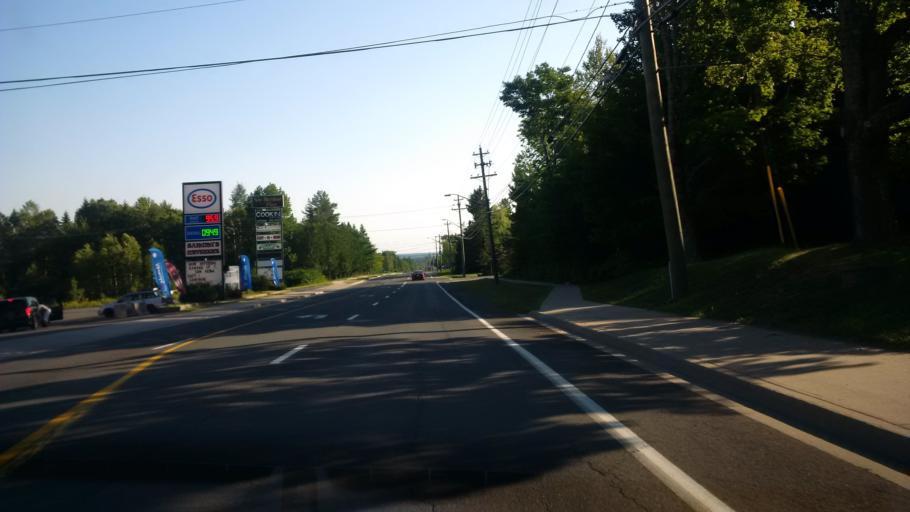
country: CA
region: New Brunswick
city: Fredericton
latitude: 45.8890
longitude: -66.6862
